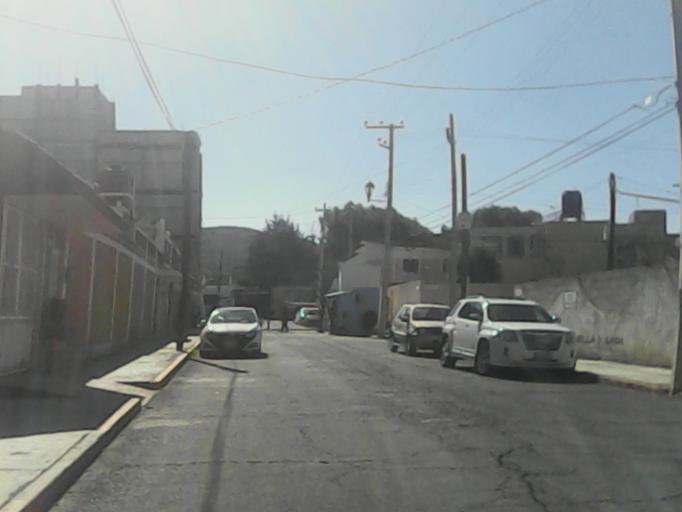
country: MX
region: Hidalgo
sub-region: Mineral de la Reforma
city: Campestre Villas del Alamo
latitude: 20.0975
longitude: -98.7138
